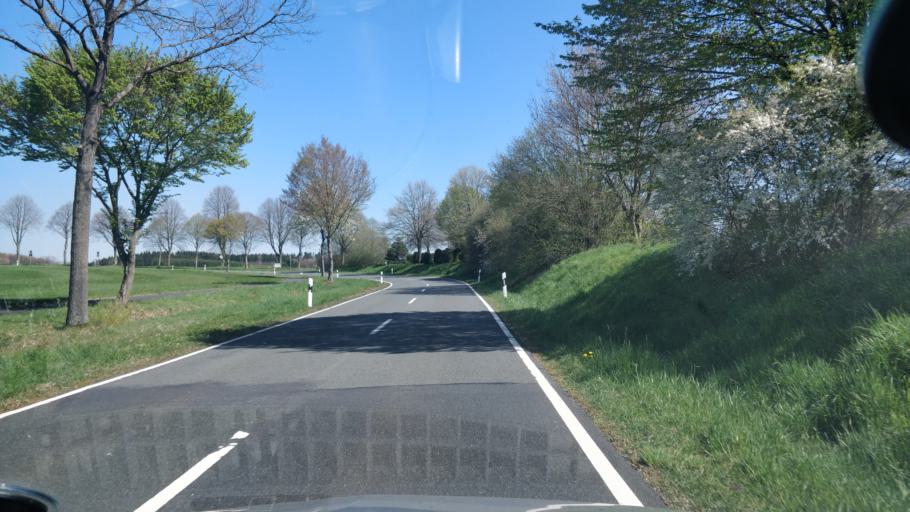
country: DE
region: Rheinland-Pfalz
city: Winnen
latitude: 50.5738
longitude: 8.0052
